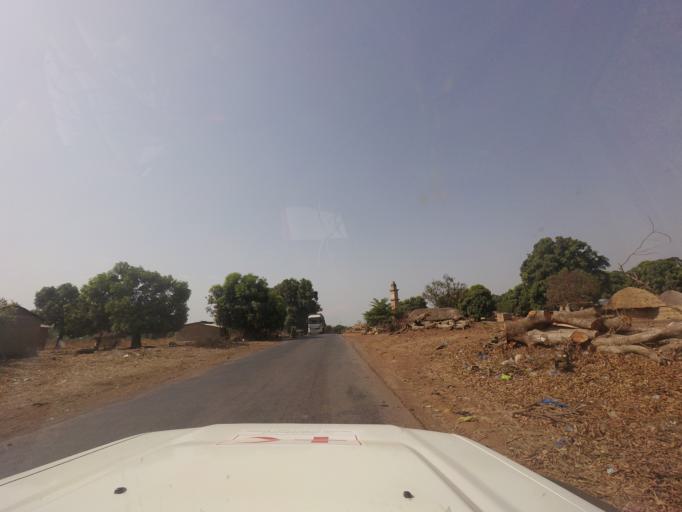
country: GN
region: Mamou
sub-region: Mamou Prefecture
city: Mamou
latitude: 10.2320
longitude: -12.4569
